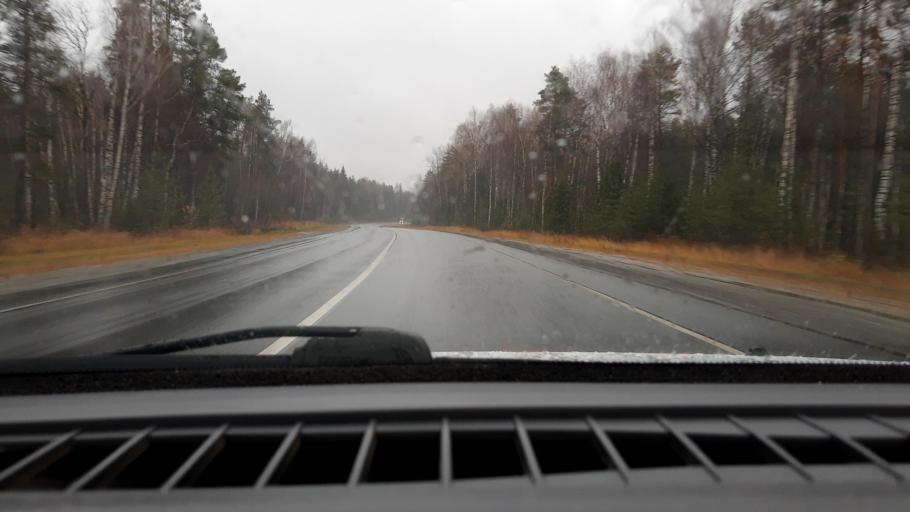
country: RU
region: Nizjnij Novgorod
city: Linda
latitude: 56.6369
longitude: 44.1045
